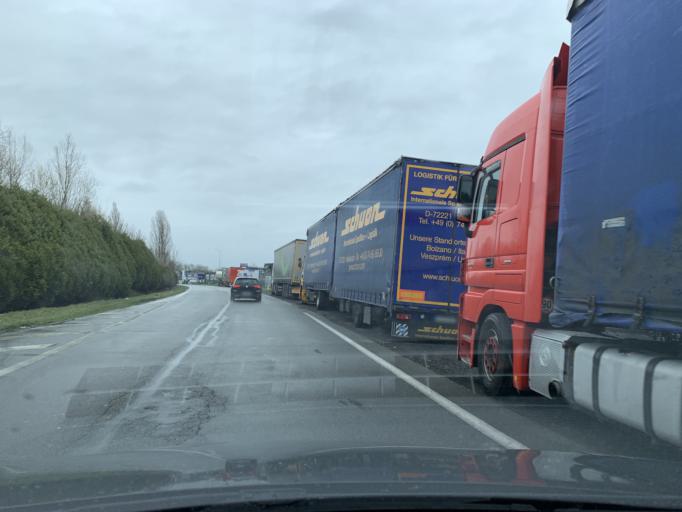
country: FR
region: Nord-Pas-de-Calais
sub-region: Departement du Nord
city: Herin
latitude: 50.3372
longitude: 3.4648
